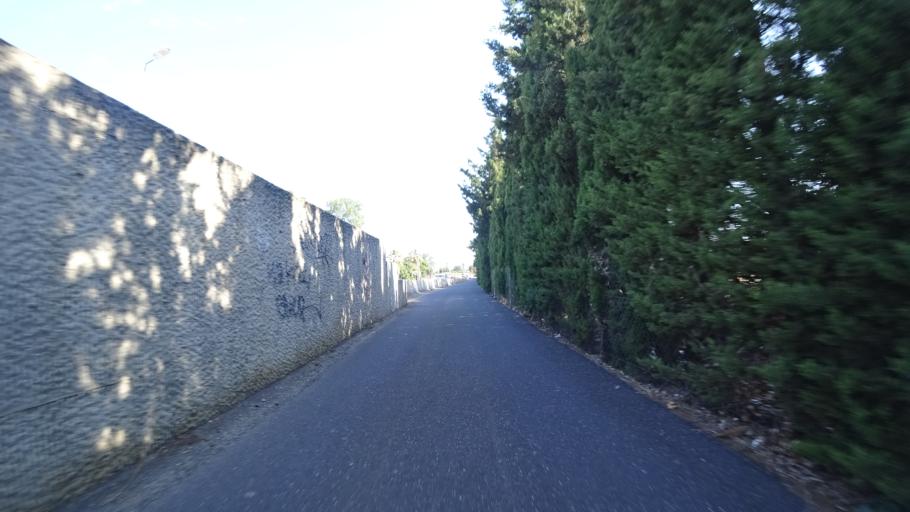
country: FR
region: Languedoc-Roussillon
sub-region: Departement des Pyrenees-Orientales
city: Perpignan
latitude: 42.7053
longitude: 2.9091
